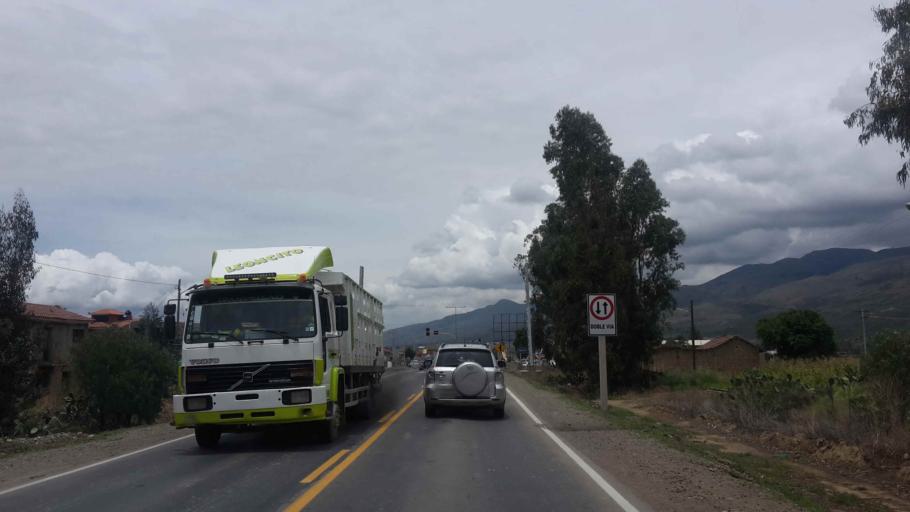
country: BO
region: Cochabamba
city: Punata
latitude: -17.5147
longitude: -65.8310
